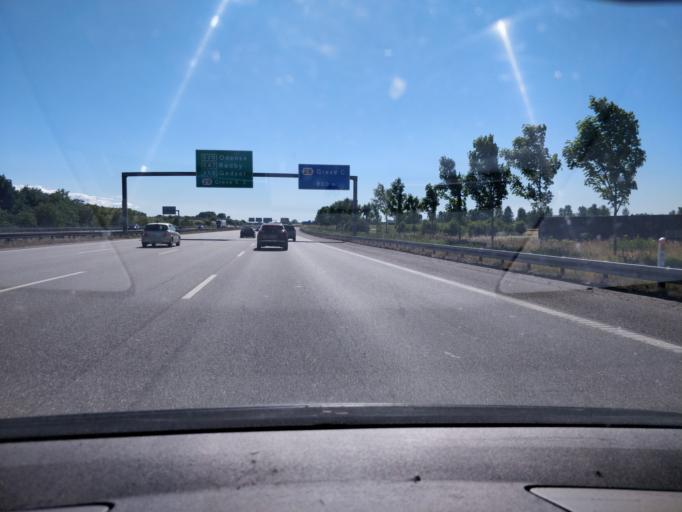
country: DK
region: Zealand
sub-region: Greve Kommune
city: Greve
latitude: 55.5993
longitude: 12.2937
